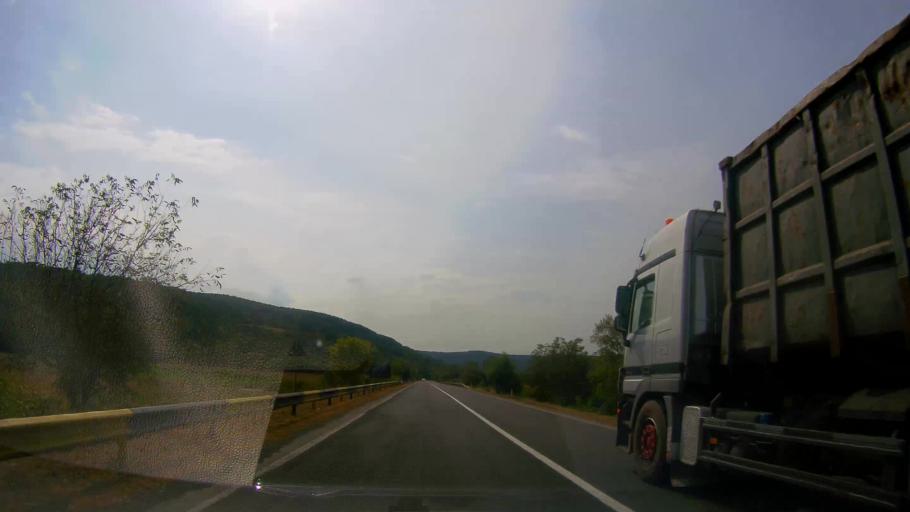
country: RO
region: Salaj
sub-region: Comuna Zimbor
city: Zimbor
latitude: 46.9933
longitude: 23.2505
